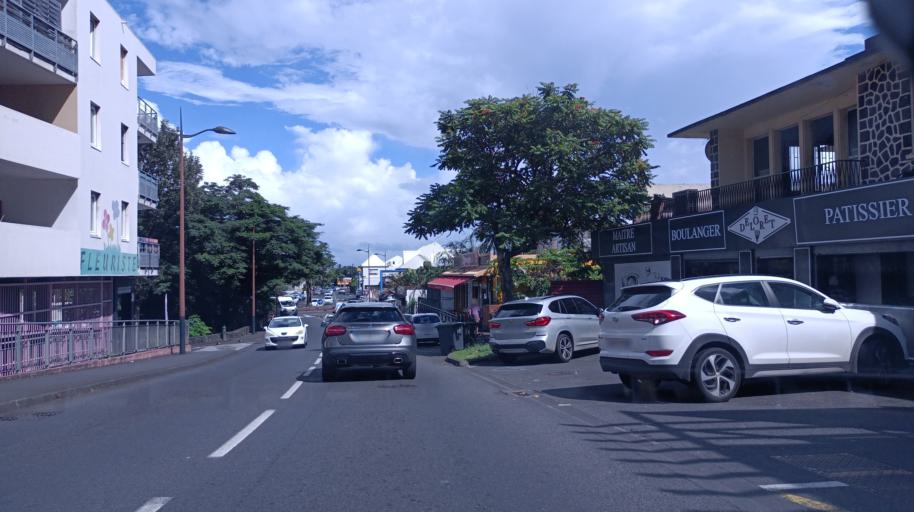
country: RE
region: Reunion
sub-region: Reunion
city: Saint-Joseph
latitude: -21.3808
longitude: 55.6140
